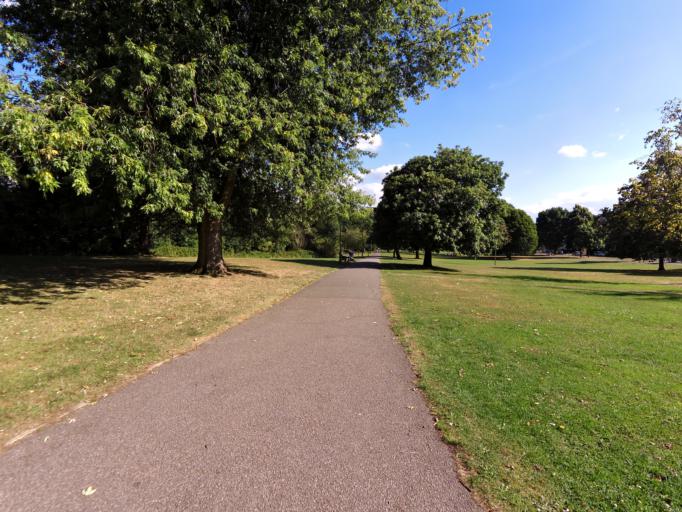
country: GB
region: England
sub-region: Greater London
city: Hadley Wood
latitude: 51.6403
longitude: -0.1610
